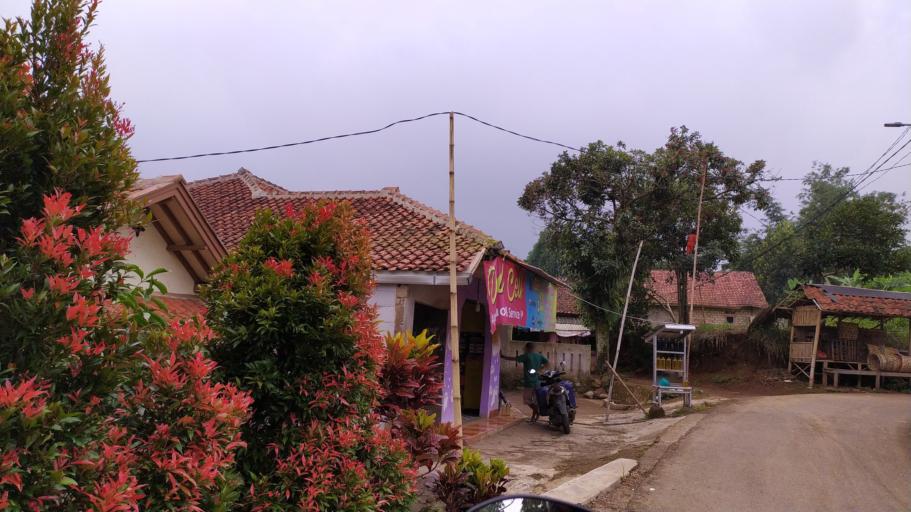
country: ID
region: West Java
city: Ciampea
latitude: -6.6301
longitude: 106.7059
